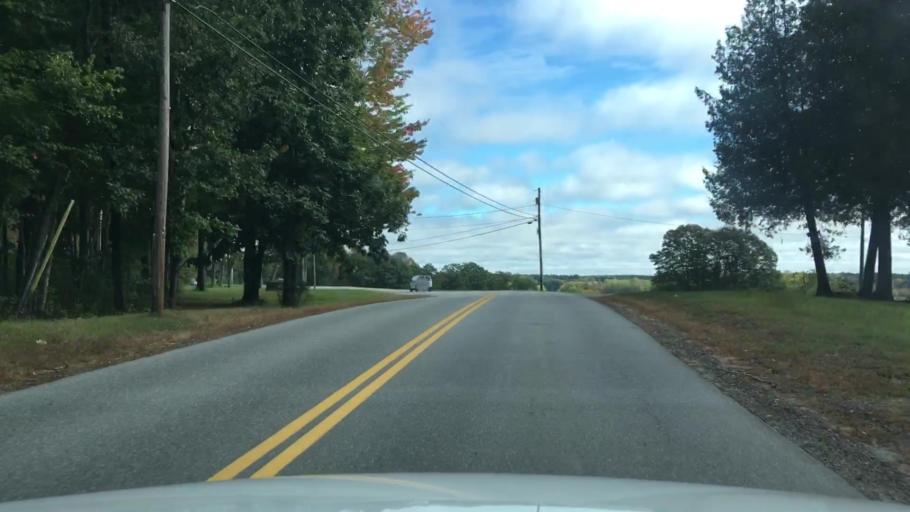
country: US
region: Maine
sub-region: Cumberland County
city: Brunswick
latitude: 43.9244
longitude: -69.9188
